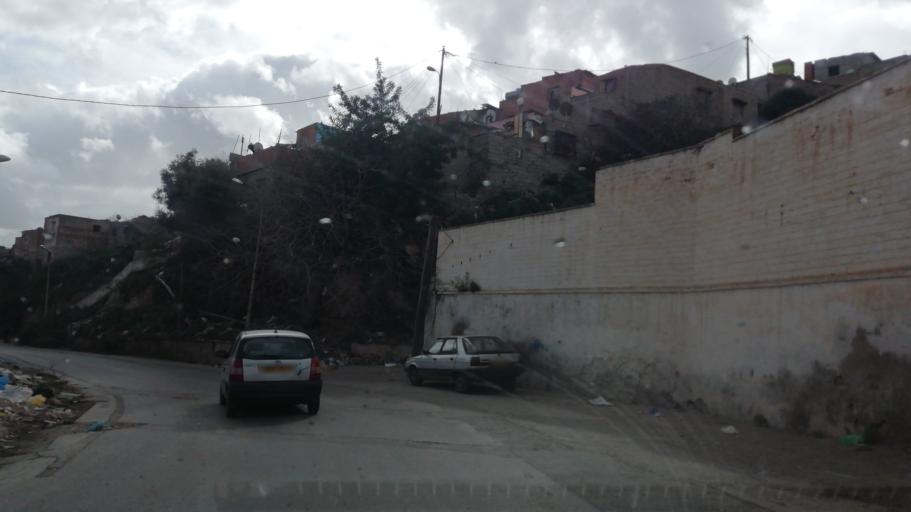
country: DZ
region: Oran
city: Oran
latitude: 35.6981
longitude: -0.6619
